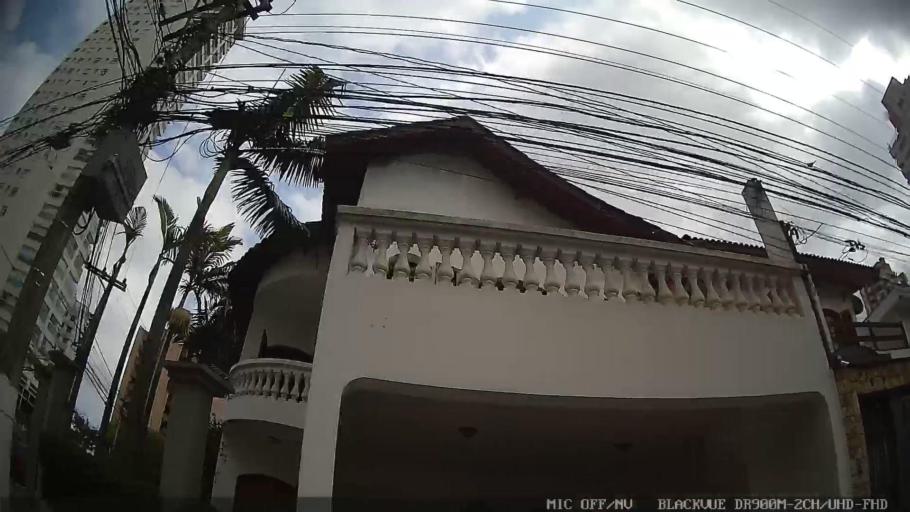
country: BR
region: Sao Paulo
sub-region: Sao Paulo
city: Sao Paulo
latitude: -23.5942
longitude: -46.6257
